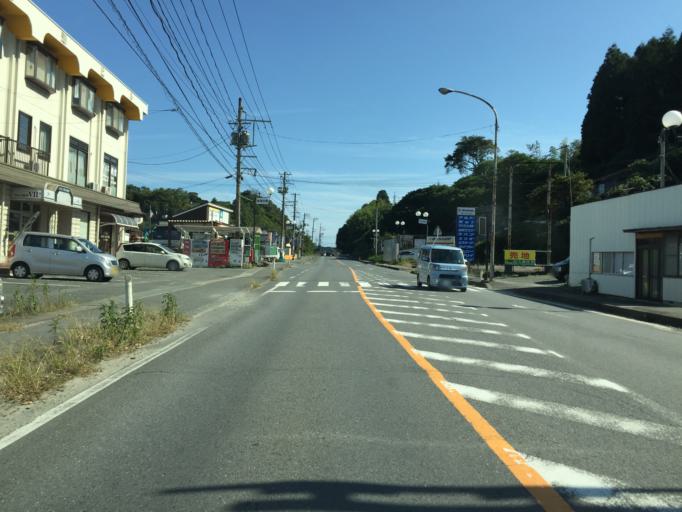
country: JP
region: Fukushima
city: Iwaki
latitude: 37.0573
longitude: 140.8721
